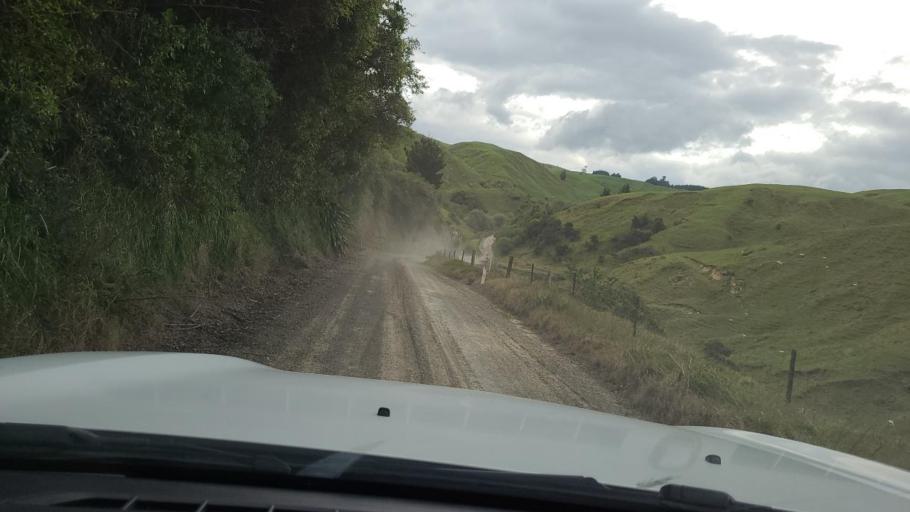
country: NZ
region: Hawke's Bay
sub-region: Napier City
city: Napier
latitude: -39.2764
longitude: 176.8388
